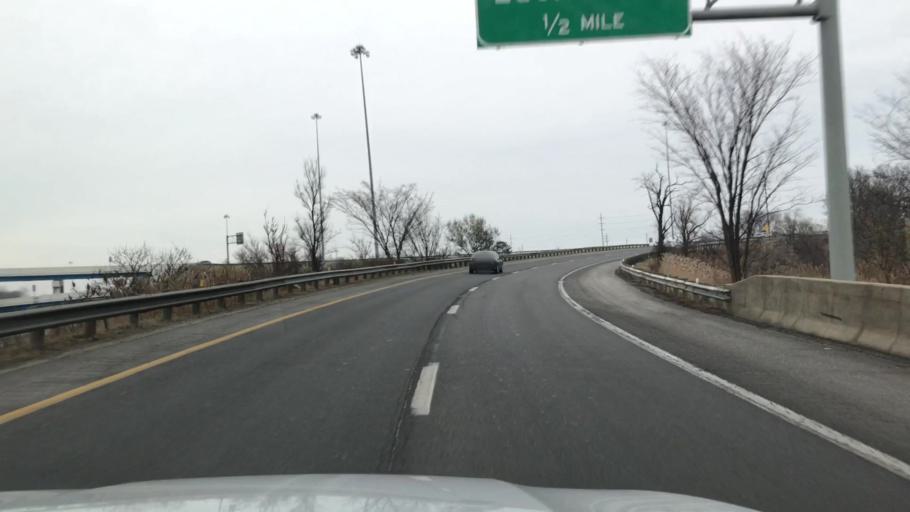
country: US
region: Ohio
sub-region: Cuyahoga County
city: Euclid
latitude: 41.6044
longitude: -81.4961
